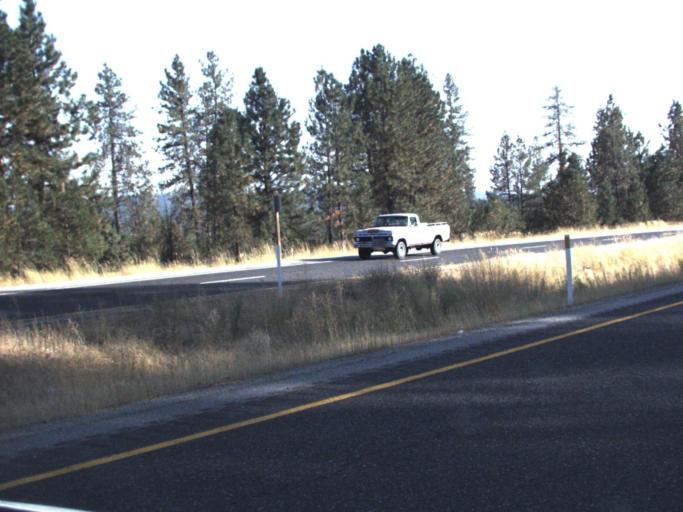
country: US
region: Washington
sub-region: Spokane County
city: Deer Park
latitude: 47.9107
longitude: -117.3504
